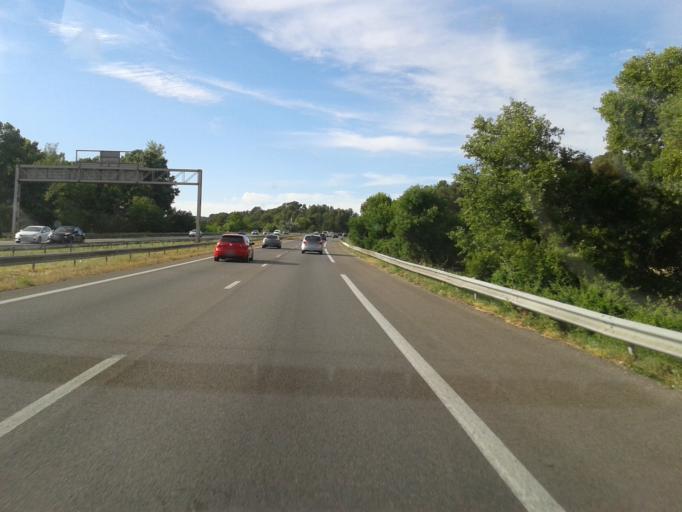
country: FR
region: Provence-Alpes-Cote d'Azur
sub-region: Departement des Bouches-du-Rhone
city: Bouc-Bel-Air
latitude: 43.4957
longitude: 5.4065
